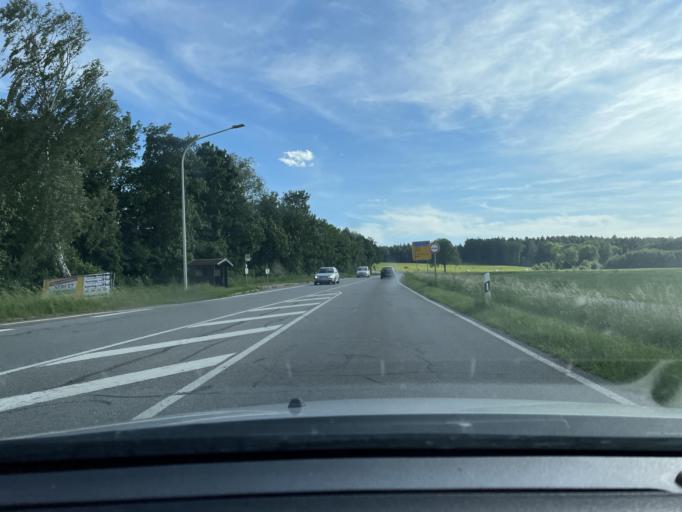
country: DE
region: Bavaria
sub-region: Lower Bavaria
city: Abensberg
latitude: 48.8063
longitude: 11.8402
